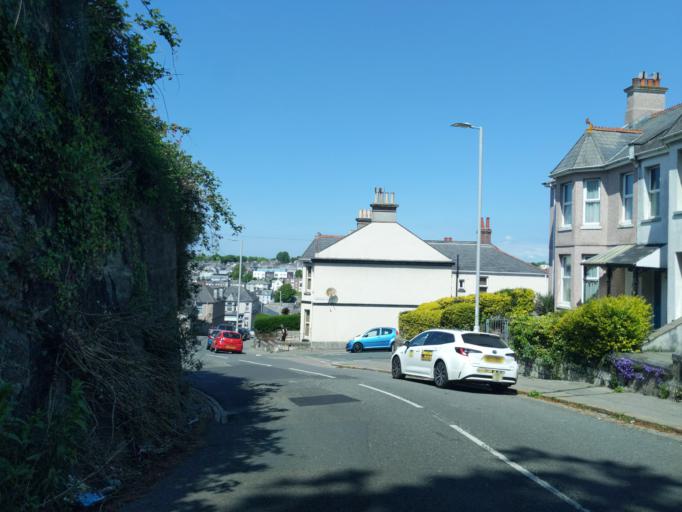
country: GB
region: England
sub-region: Cornwall
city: Millbrook
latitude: 50.3827
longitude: -4.1650
